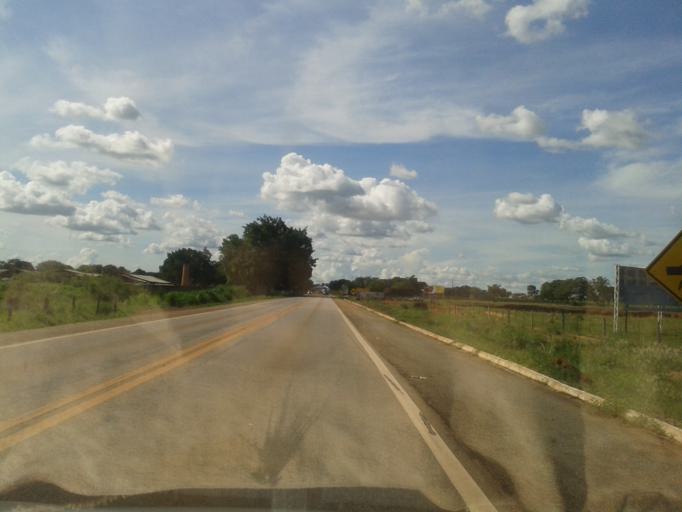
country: BR
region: Goias
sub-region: Mozarlandia
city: Mozarlandia
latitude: -15.1060
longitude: -50.6098
